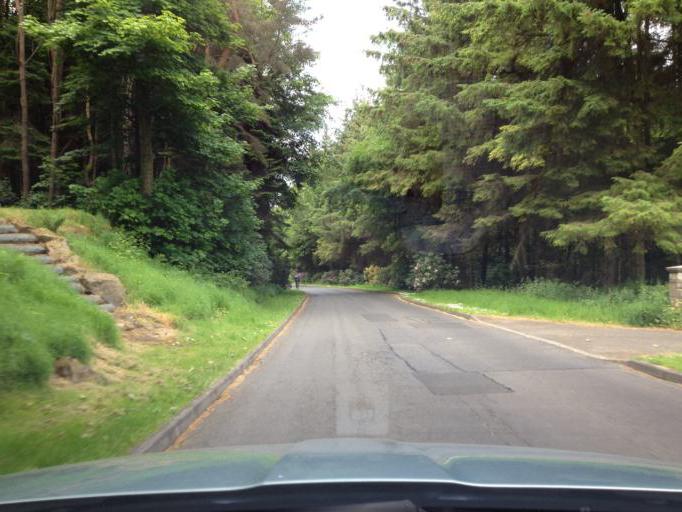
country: GB
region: Scotland
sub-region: Fife
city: Strathkinness
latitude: 56.3213
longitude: -2.8500
